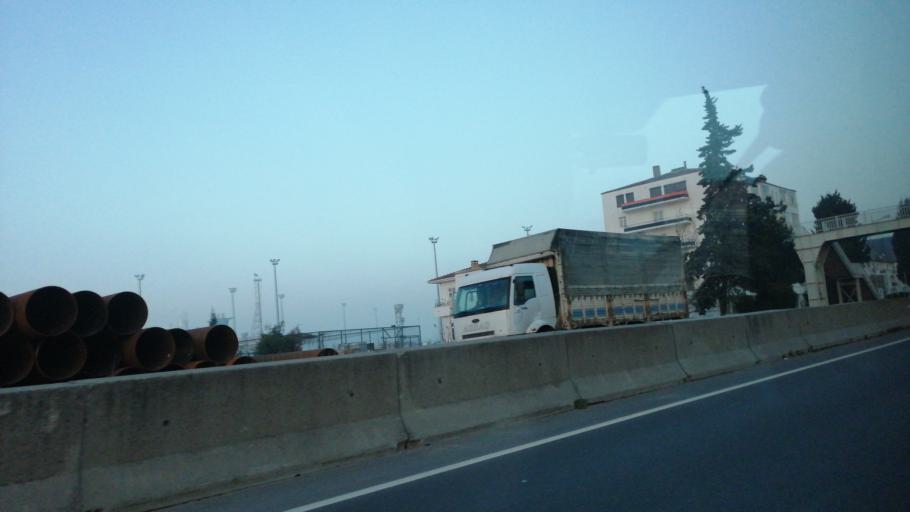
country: TR
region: Yalova
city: Taskopru
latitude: 40.6878
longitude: 29.4278
